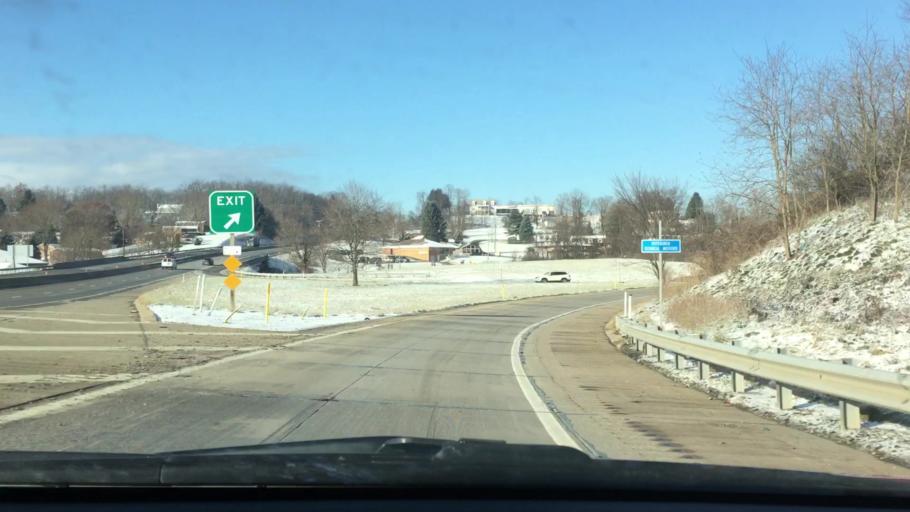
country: US
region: Pennsylvania
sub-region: Allegheny County
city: Enlow
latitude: 40.4371
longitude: -80.2082
